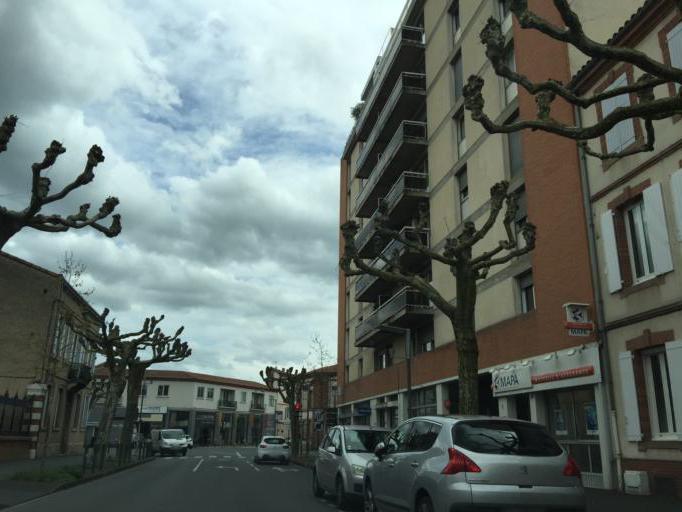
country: FR
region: Midi-Pyrenees
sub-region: Departement du Tarn
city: Albi
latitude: 43.9228
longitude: 2.1463
